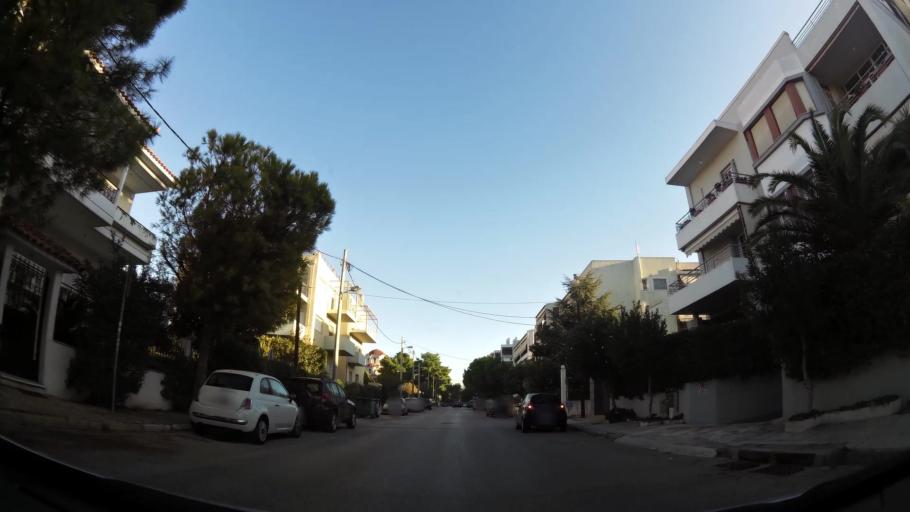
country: GR
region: Attica
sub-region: Nomarchia Athinas
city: Marousi
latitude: 38.0457
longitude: 23.7979
